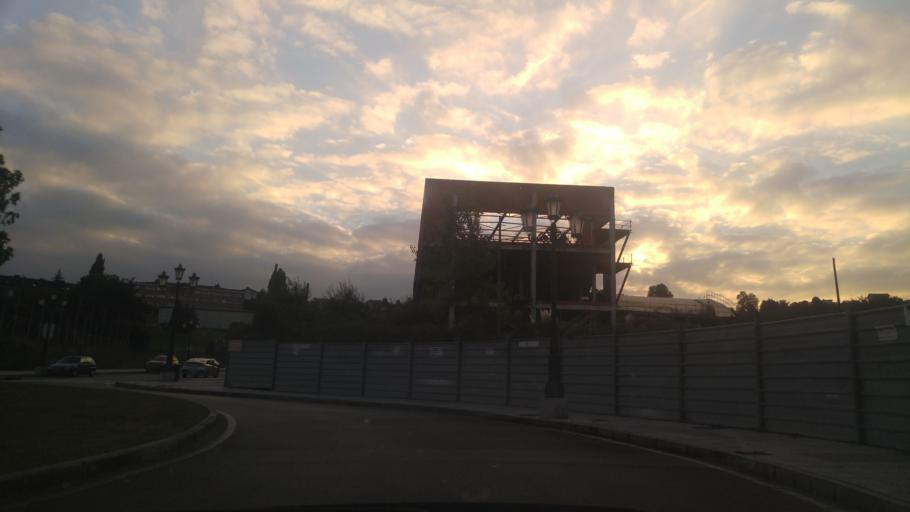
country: ES
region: Asturias
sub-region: Province of Asturias
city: Oviedo
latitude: 43.3746
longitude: -5.8569
